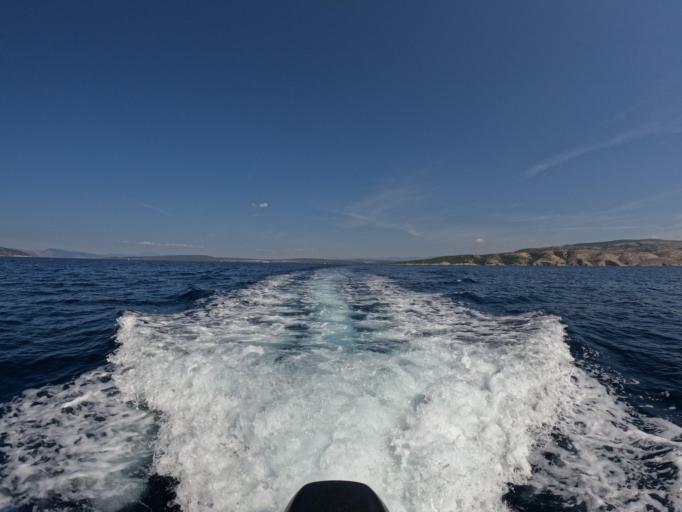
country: HR
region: Primorsko-Goranska
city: Punat
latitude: 44.9512
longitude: 14.6120
